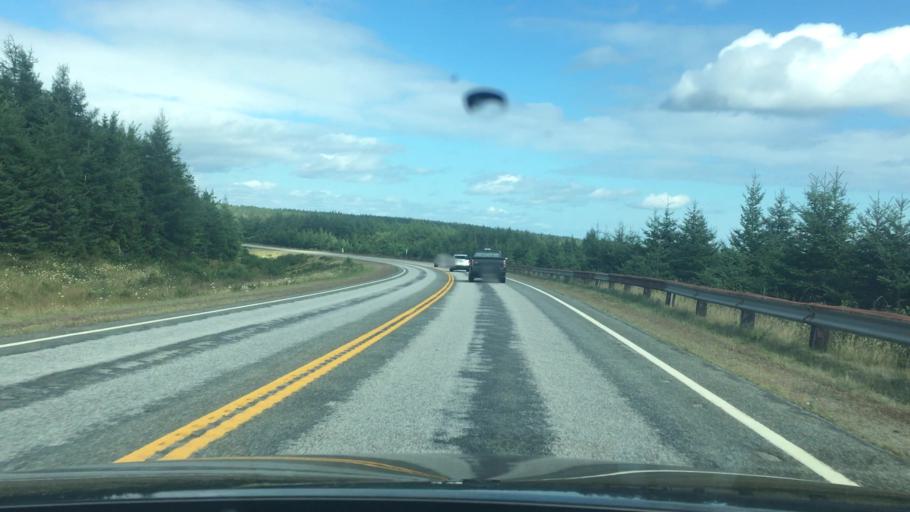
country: CA
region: Nova Scotia
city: Princeville
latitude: 45.6119
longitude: -61.0619
